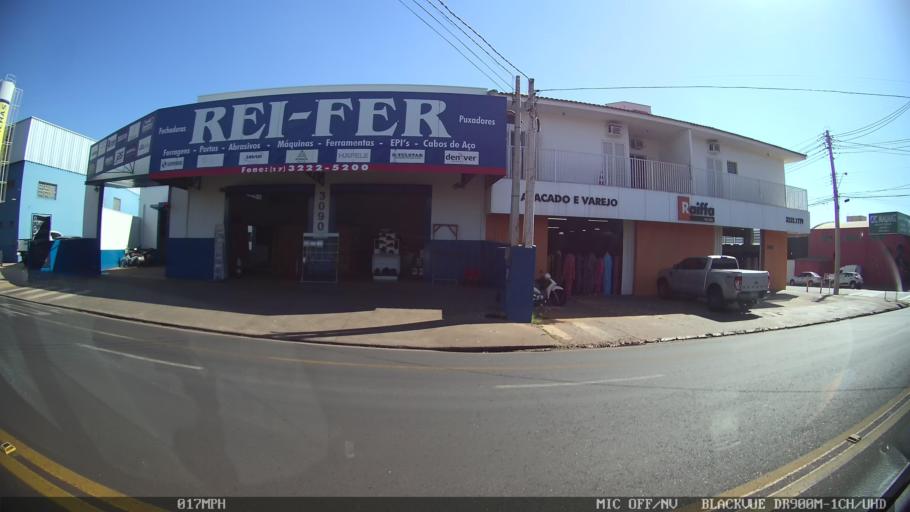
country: BR
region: Sao Paulo
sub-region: Sao Jose Do Rio Preto
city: Sao Jose do Rio Preto
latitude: -20.8077
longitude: -49.4041
